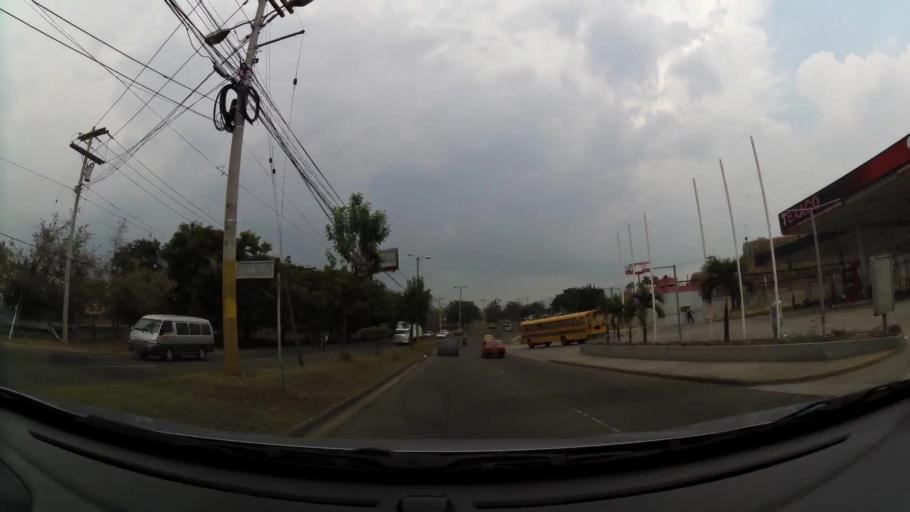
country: HN
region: Francisco Morazan
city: Tegucigalpa
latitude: 14.0760
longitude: -87.1987
